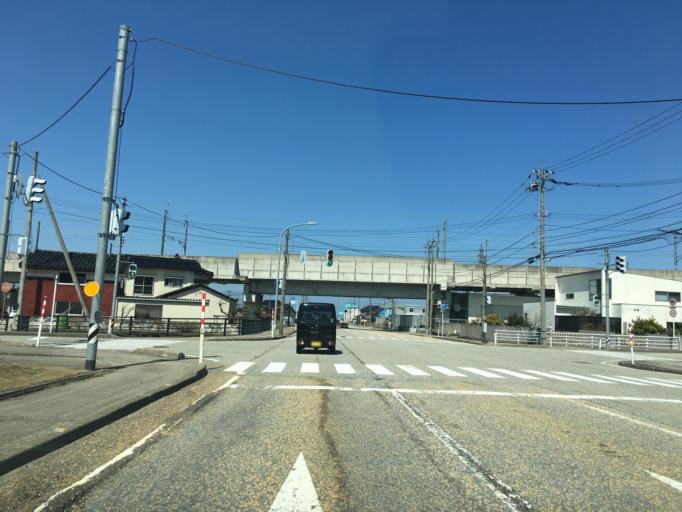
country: JP
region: Toyama
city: Namerikawa
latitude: 36.7530
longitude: 137.3658
